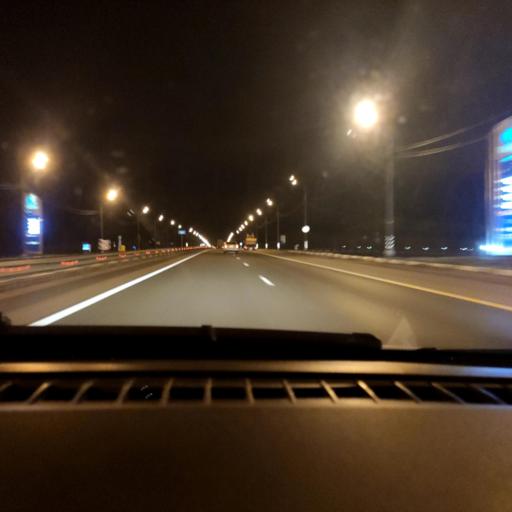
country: RU
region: Lipetsk
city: Khlevnoye
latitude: 52.2305
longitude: 39.0917
